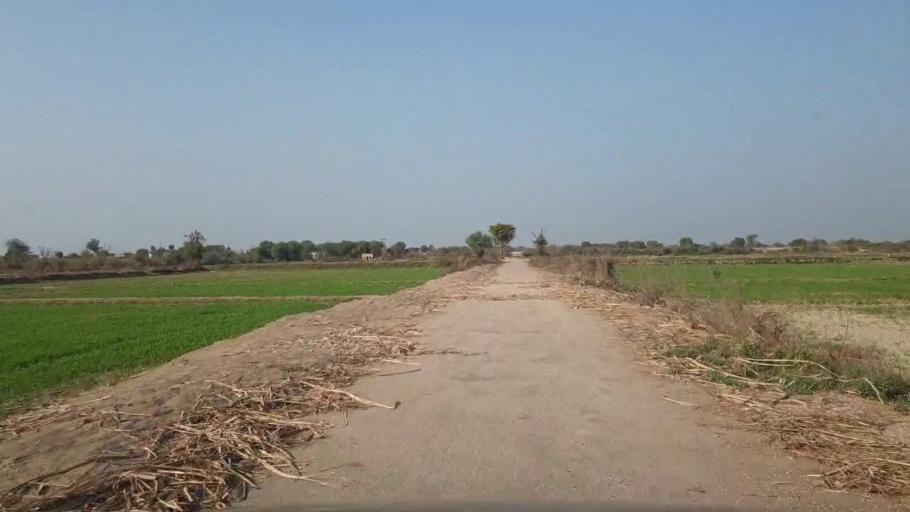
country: PK
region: Sindh
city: Hala
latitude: 25.8569
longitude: 68.3565
